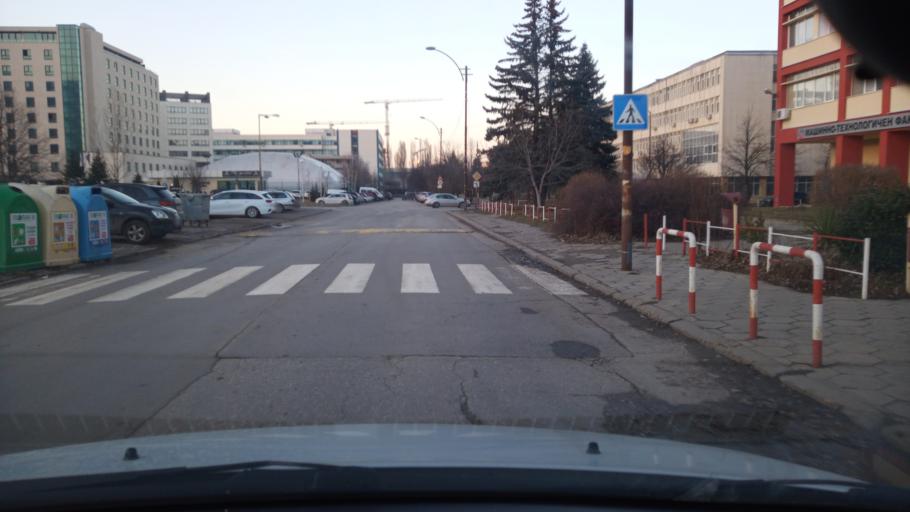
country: BG
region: Sofia-Capital
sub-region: Stolichna Obshtina
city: Sofia
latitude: 42.6555
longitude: 23.3538
